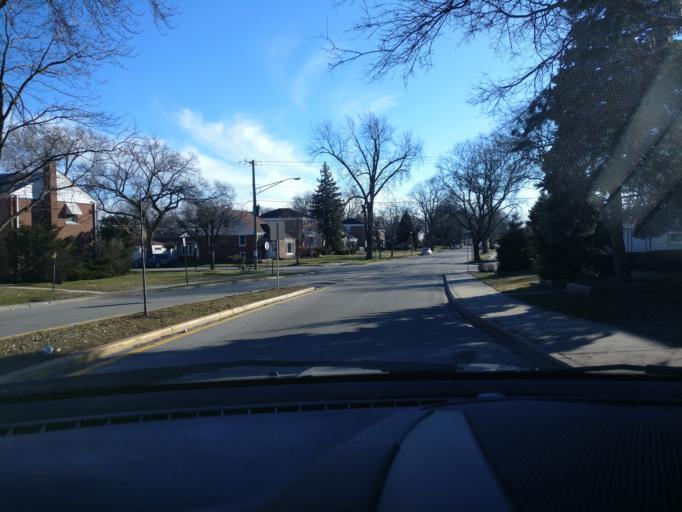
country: US
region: Illinois
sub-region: Cook County
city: Skokie
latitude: 42.0395
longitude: -87.7570
